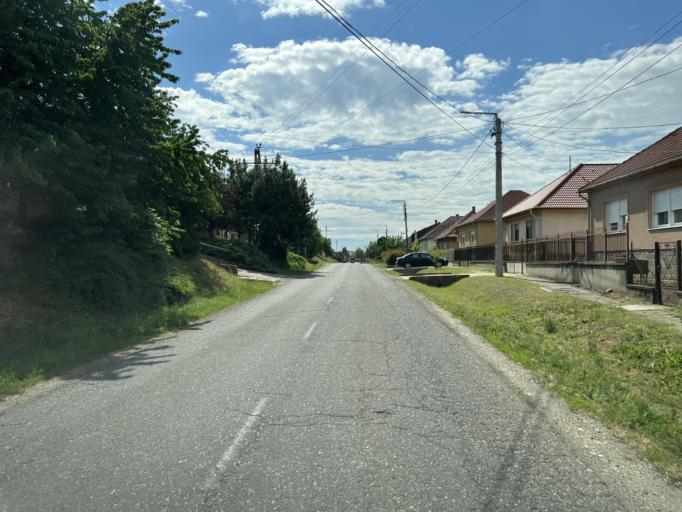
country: HU
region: Pest
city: Zsambok
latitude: 47.5482
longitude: 19.6009
